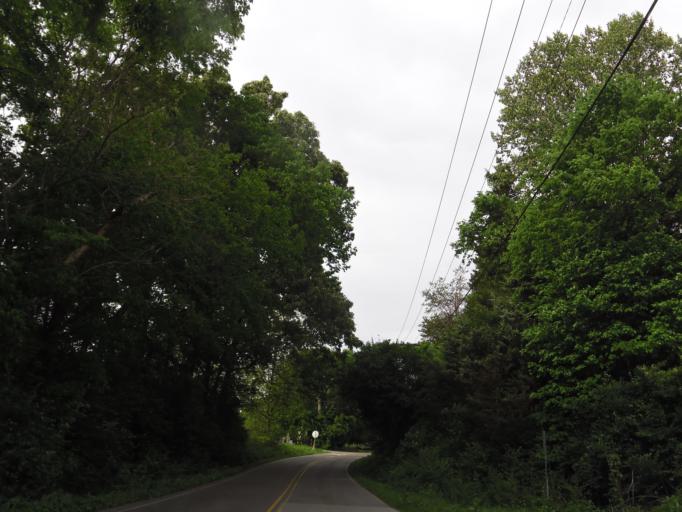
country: US
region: Tennessee
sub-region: Knox County
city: Knoxville
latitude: 36.0214
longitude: -83.8567
